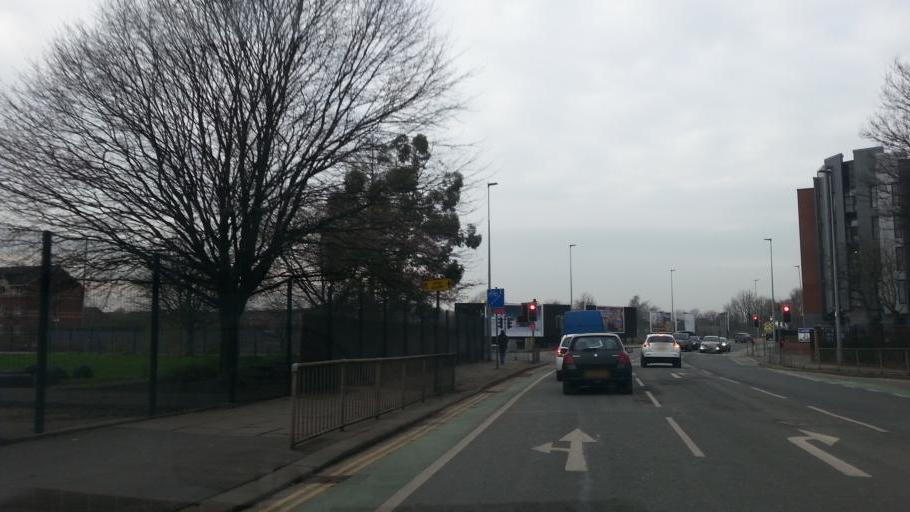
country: GB
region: England
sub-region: Manchester
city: Cheetham Hill
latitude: 53.4893
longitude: -2.2582
